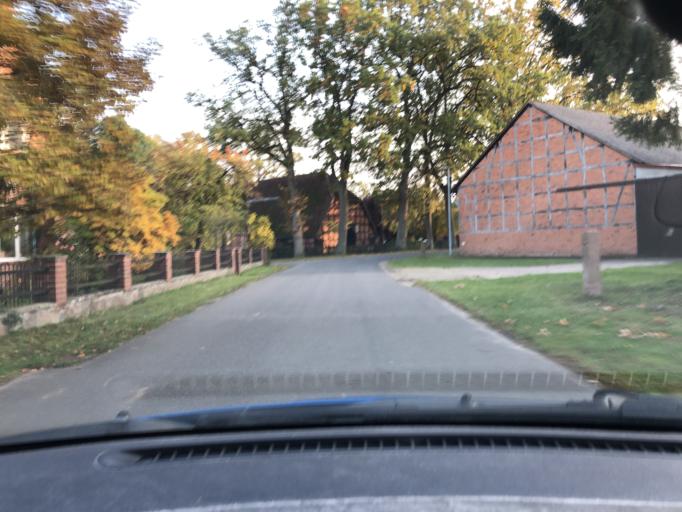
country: DE
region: Lower Saxony
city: Gohrde
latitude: 53.1371
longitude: 10.9539
